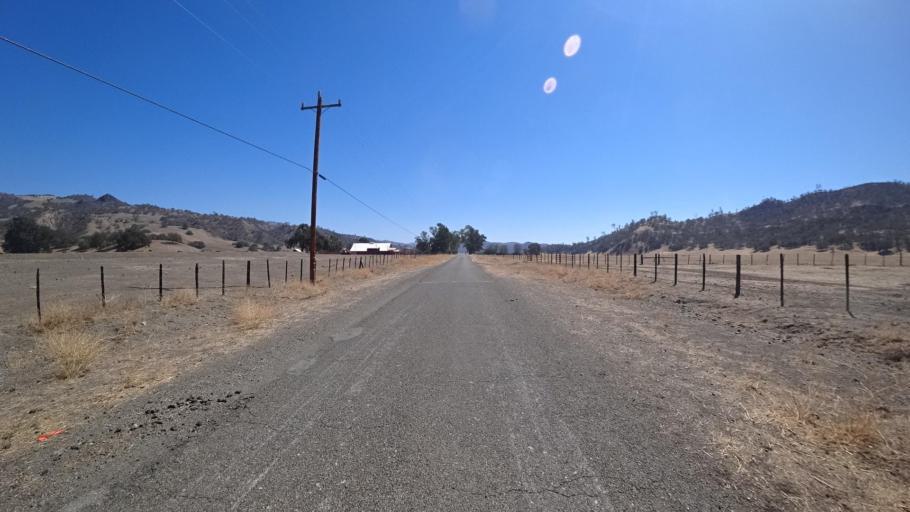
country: US
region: California
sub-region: San Luis Obispo County
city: San Miguel
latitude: 36.1134
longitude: -120.7229
